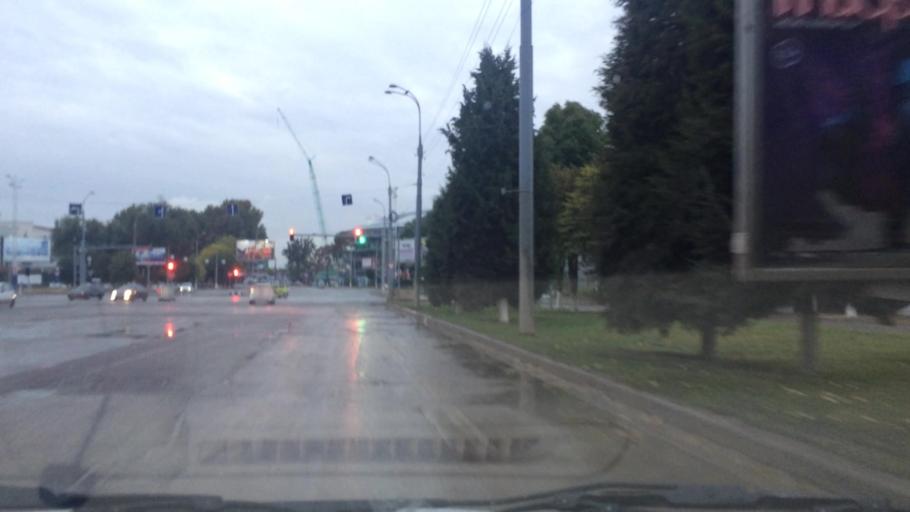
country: UZ
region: Toshkent Shahri
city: Tashkent
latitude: 41.3122
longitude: 69.2533
